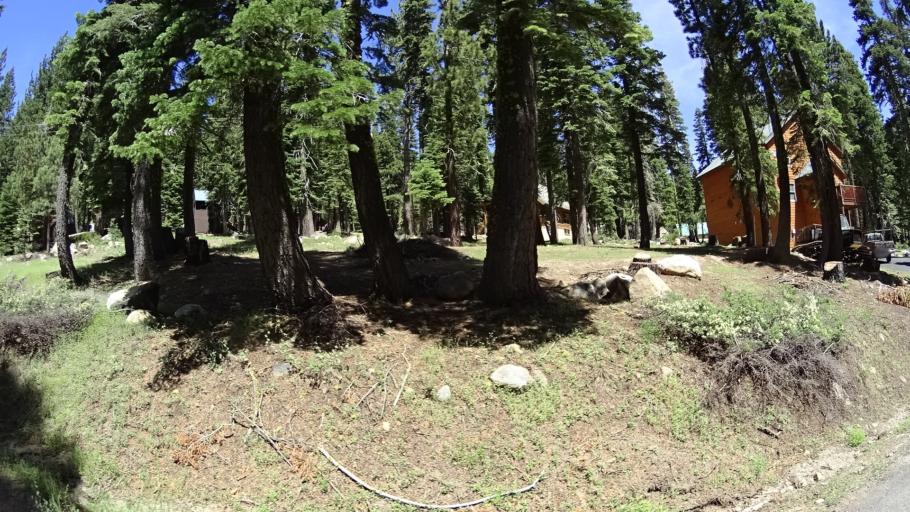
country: US
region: California
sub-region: Calaveras County
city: Arnold
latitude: 38.4274
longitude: -120.0998
